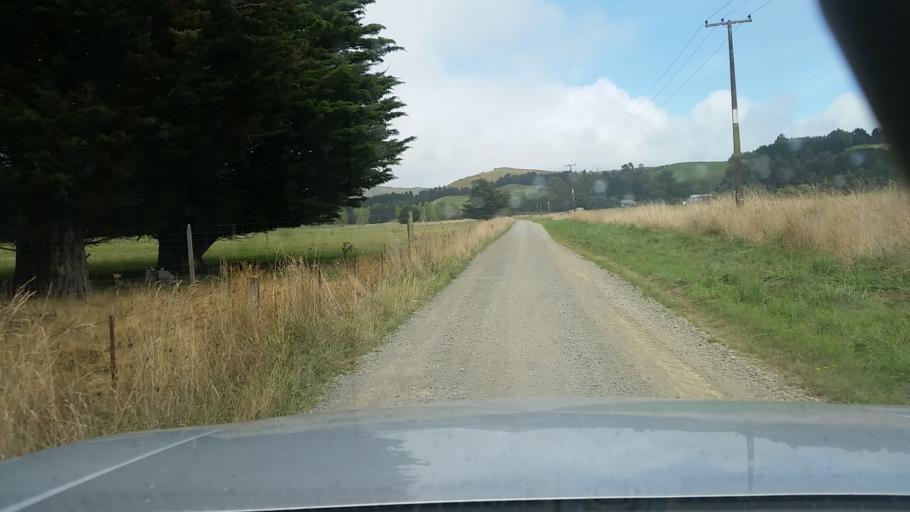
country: NZ
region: Marlborough
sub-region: Marlborough District
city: Blenheim
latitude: -41.7255
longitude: 173.9250
